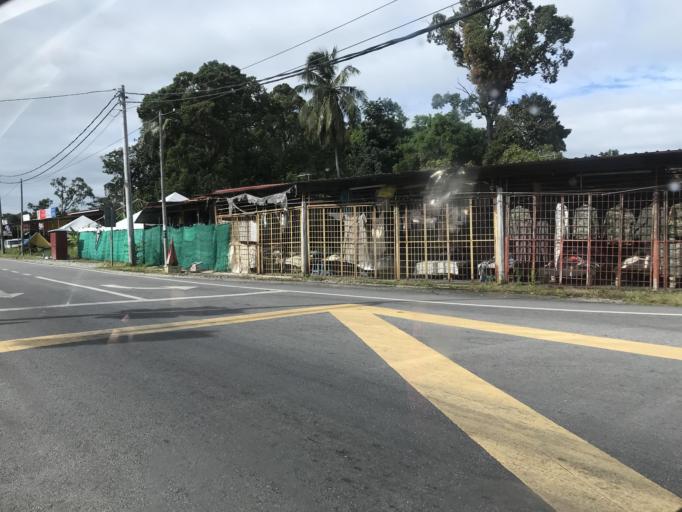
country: MY
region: Kelantan
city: Kota Bharu
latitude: 6.1317
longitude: 102.1769
